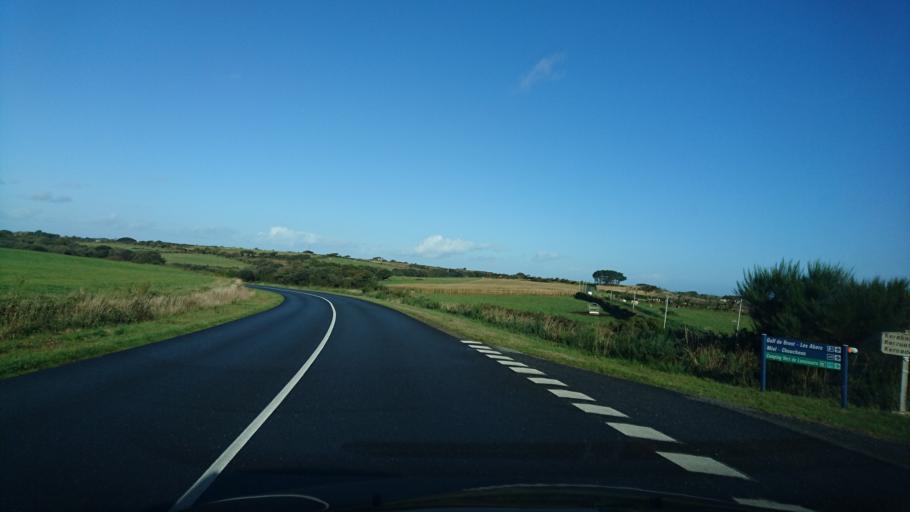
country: FR
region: Brittany
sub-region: Departement du Finistere
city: Plouarzel
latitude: 48.4375
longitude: -4.7164
